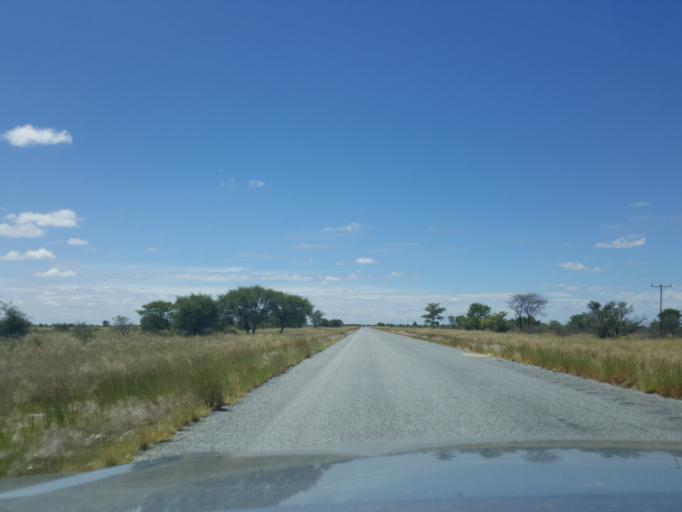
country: BW
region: Central
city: Nata
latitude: -20.1992
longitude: 26.1116
